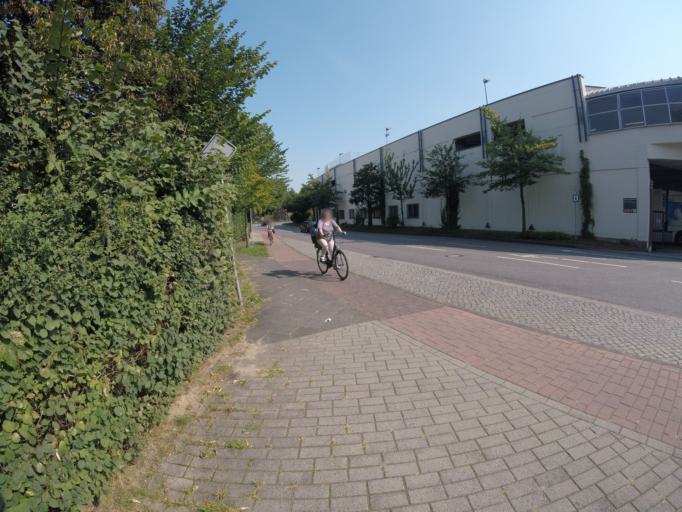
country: DE
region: Lower Saxony
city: Stade
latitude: 53.6058
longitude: 9.4763
